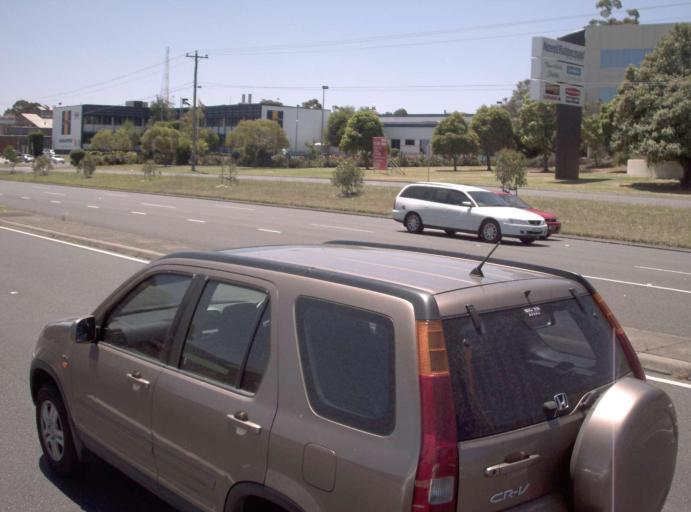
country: AU
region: Victoria
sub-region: Greater Dandenong
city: Noble Park North
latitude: -37.9560
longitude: 145.1821
